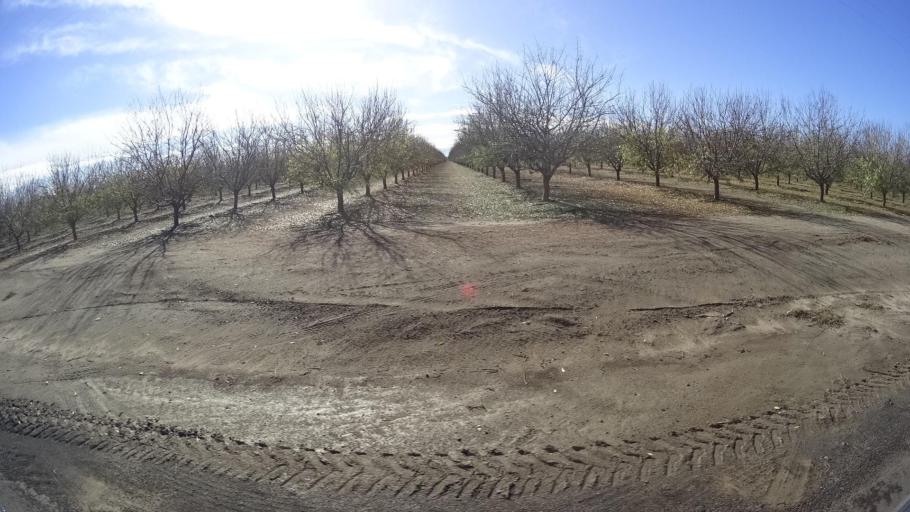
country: US
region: California
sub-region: Kern County
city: Rosedale
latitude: 35.3689
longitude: -119.2358
